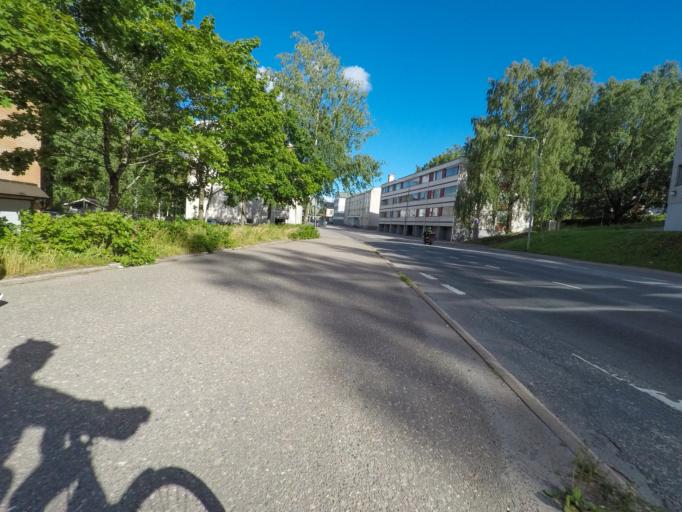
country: FI
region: South Karelia
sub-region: Lappeenranta
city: Lappeenranta
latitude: 61.0630
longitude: 28.1772
